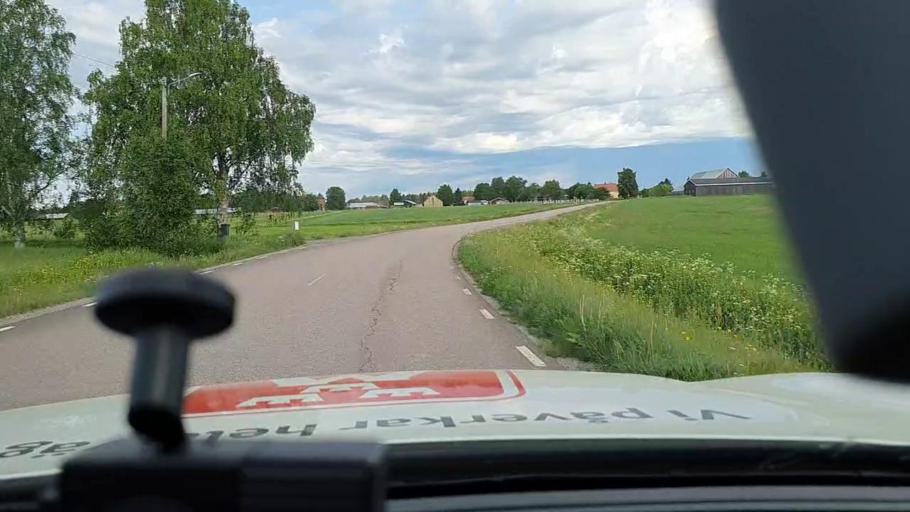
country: SE
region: Norrbotten
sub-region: Bodens Kommun
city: Saevast
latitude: 65.7062
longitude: 21.7631
